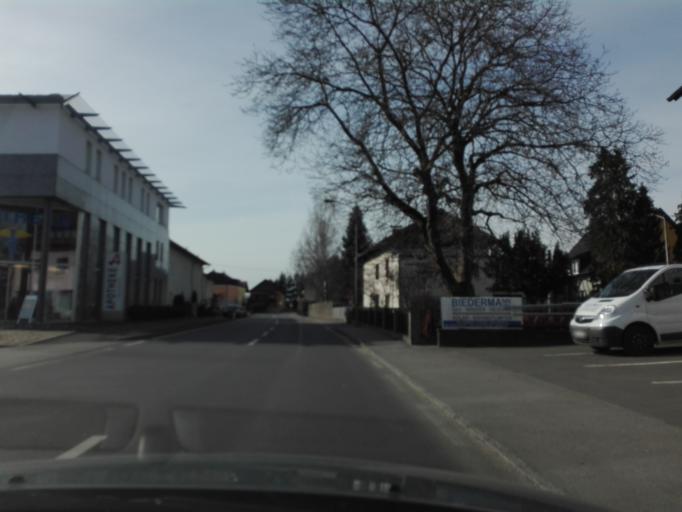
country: AT
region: Upper Austria
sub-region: Politischer Bezirk Linz-Land
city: Ansfelden
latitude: 48.2244
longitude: 14.2935
